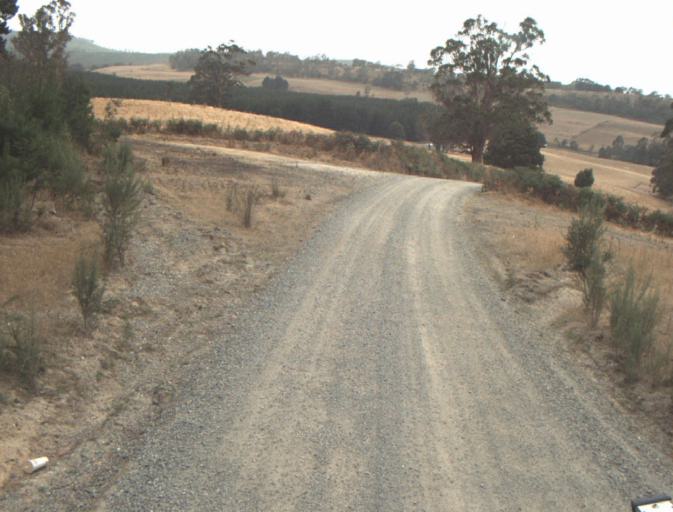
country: AU
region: Tasmania
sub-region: Launceston
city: Mayfield
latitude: -41.1724
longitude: 147.1988
